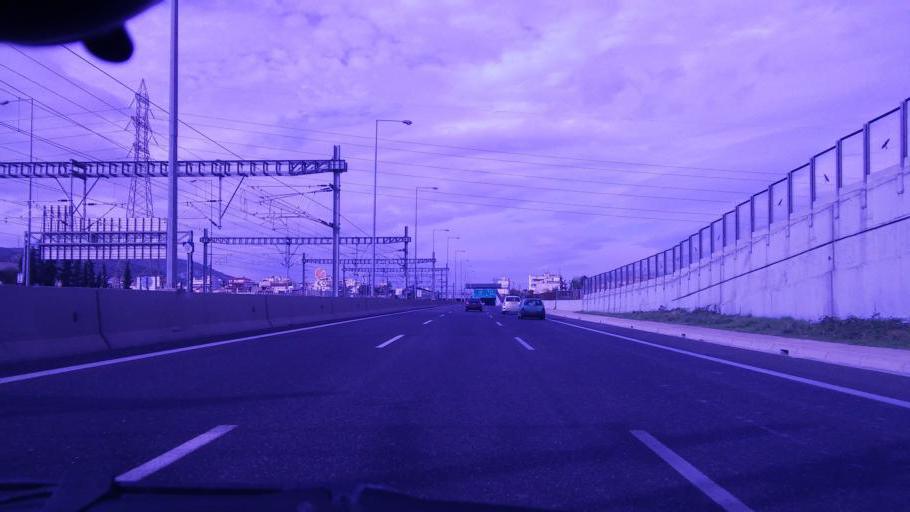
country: GR
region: Attica
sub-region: Nomarchia Dytikis Attikis
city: Zefyri
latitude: 38.0687
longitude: 23.7246
